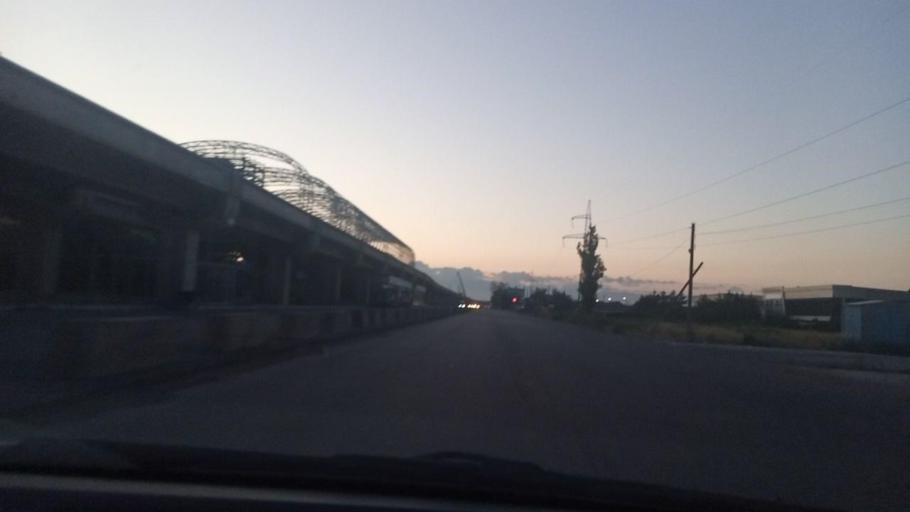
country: UZ
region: Toshkent Shahri
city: Bektemir
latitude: 41.2442
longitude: 69.2980
